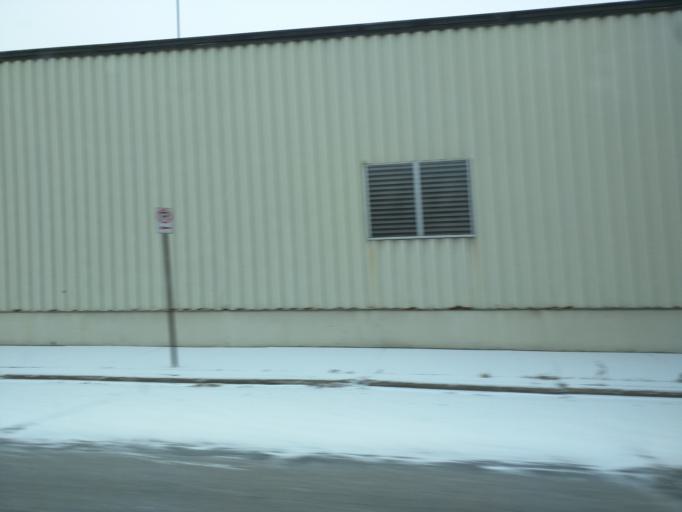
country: US
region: Wisconsin
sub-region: La Crosse County
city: La Crosse
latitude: 43.8042
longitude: -91.2535
